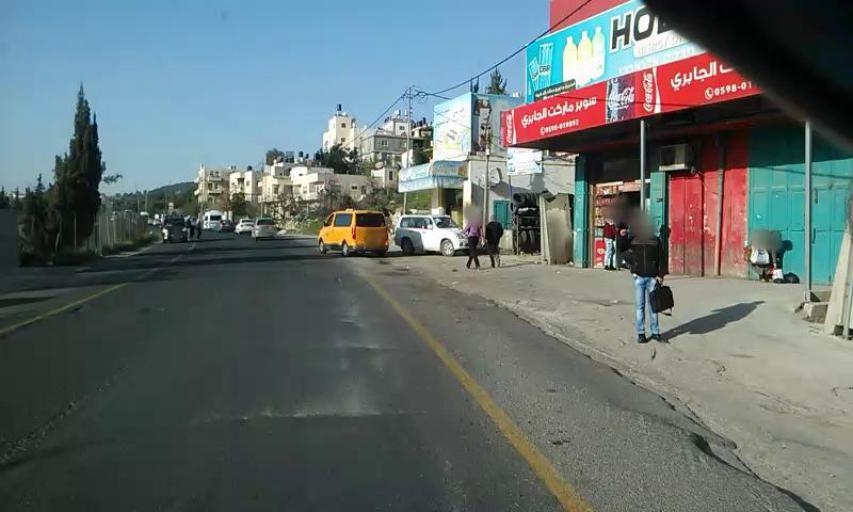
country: PS
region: West Bank
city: Shuyukh al `Arrub
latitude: 31.6261
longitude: 35.1330
